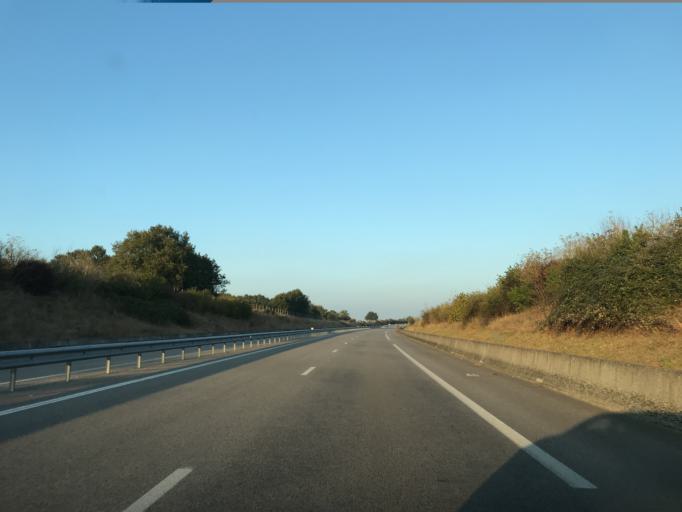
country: FR
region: Lower Normandy
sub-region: Departement de l'Orne
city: Sees
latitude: 48.4980
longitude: 0.3014
